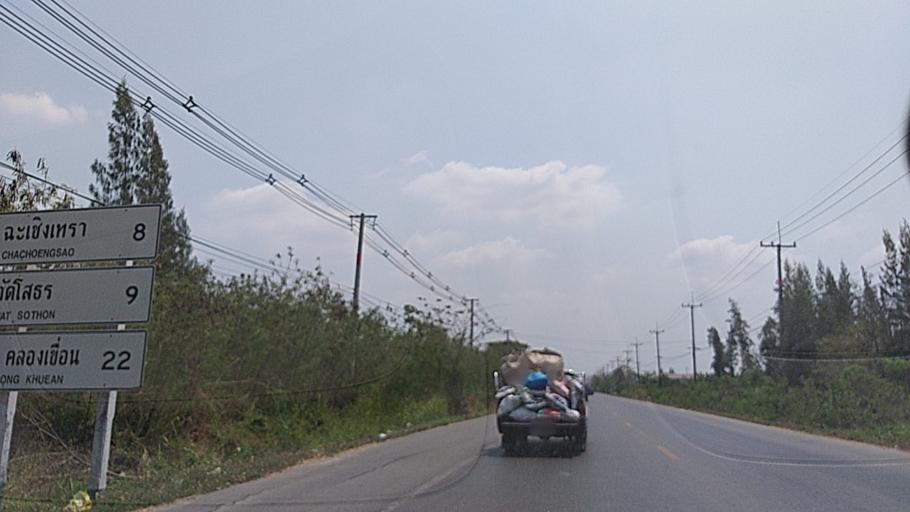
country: TH
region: Chachoengsao
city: Chachoengsao
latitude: 13.7670
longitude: 101.0691
